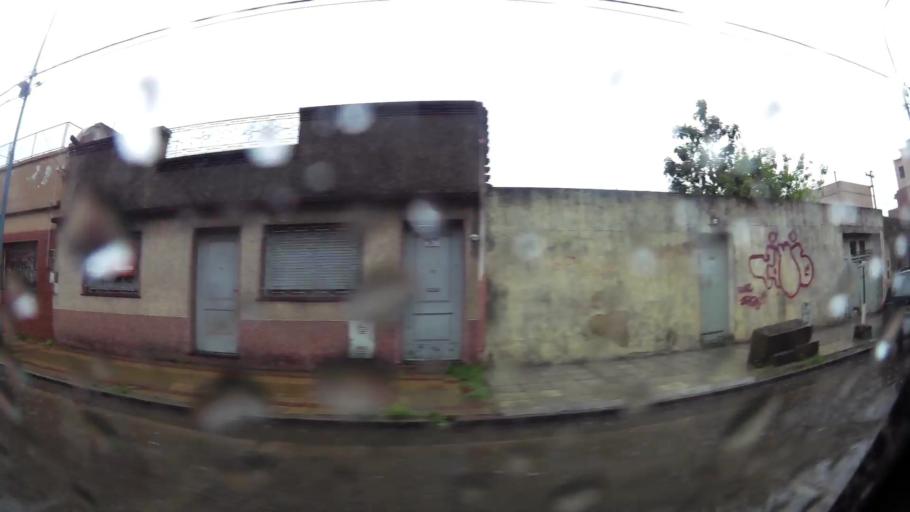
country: AR
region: Buenos Aires
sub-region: Partido de Lanus
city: Lanus
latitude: -34.7181
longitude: -58.4093
